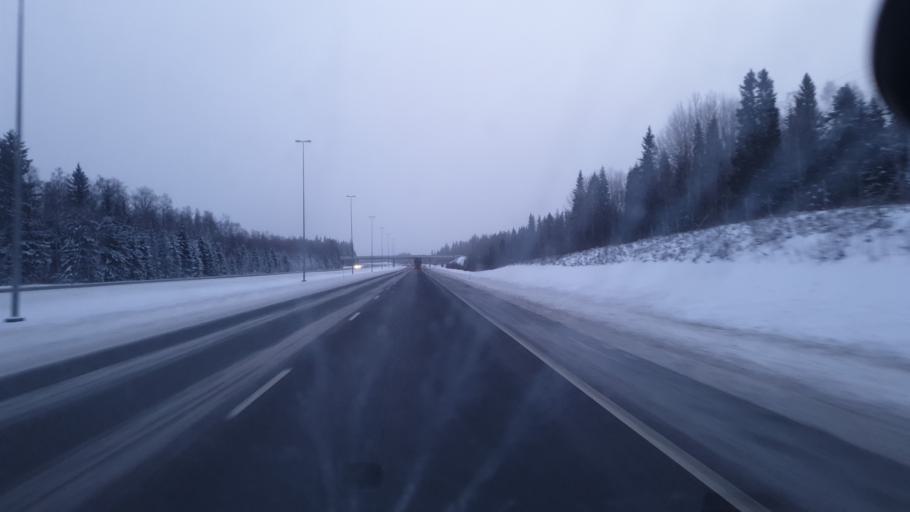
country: FI
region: Lapland
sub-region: Kemi-Tornio
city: Keminmaa
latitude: 65.8304
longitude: 24.3668
